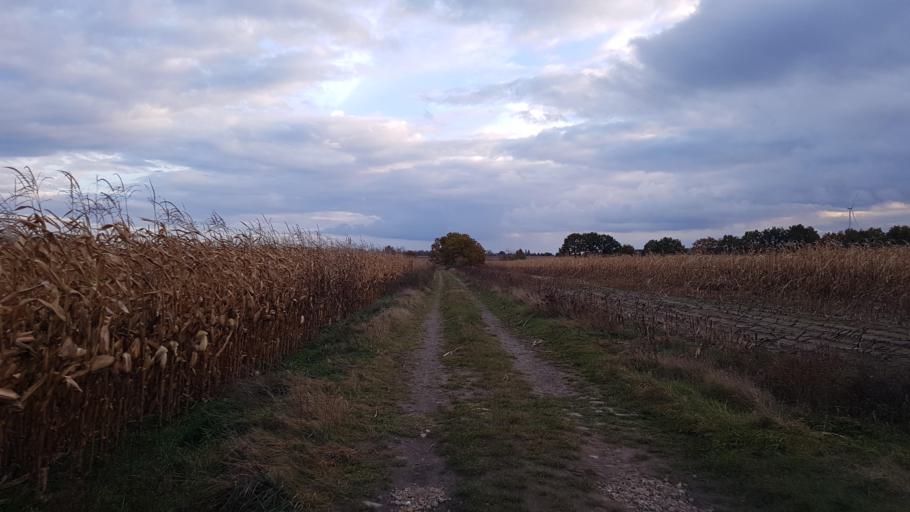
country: DE
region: Saxony-Anhalt
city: Seyda
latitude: 51.9361
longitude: 12.8786
